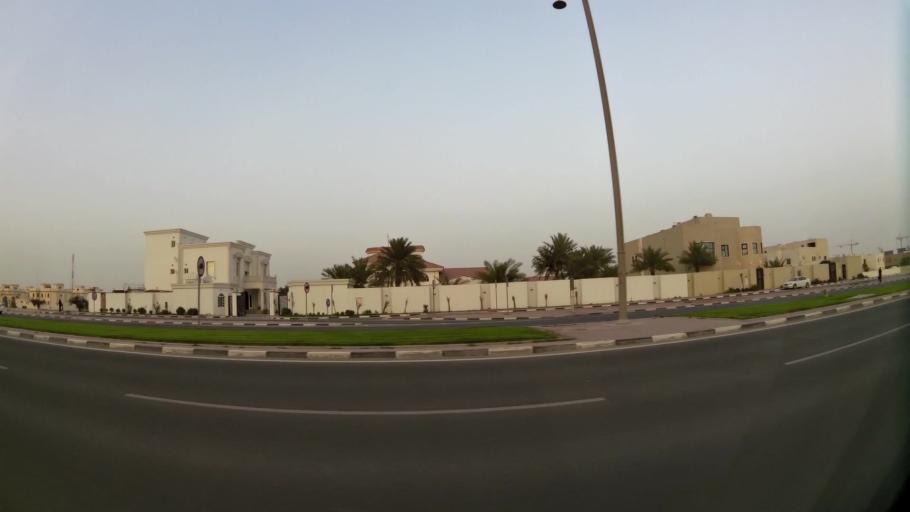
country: QA
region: Baladiyat ar Rayyan
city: Ar Rayyan
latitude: 25.2615
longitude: 51.4659
